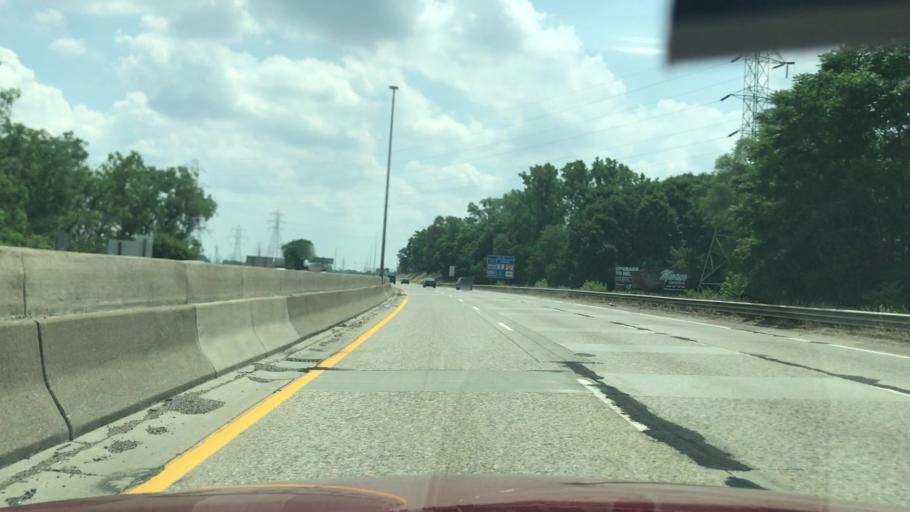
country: US
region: Michigan
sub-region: Kent County
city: Wyoming
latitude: 42.9227
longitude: -85.6819
